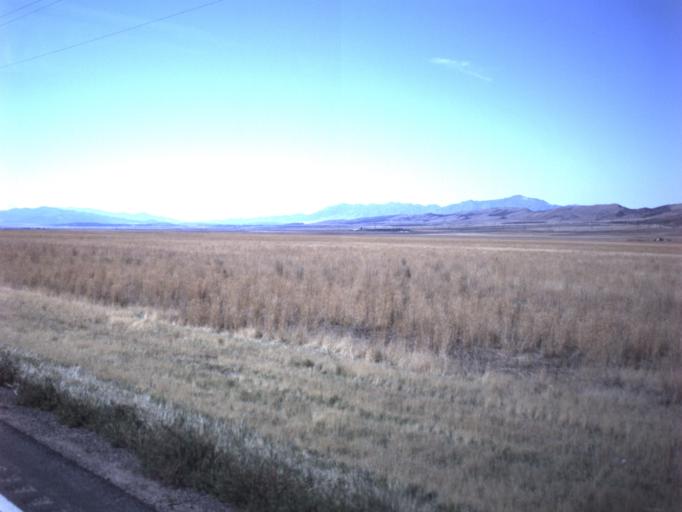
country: US
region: Utah
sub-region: Juab County
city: Nephi
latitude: 39.6229
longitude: -111.8619
